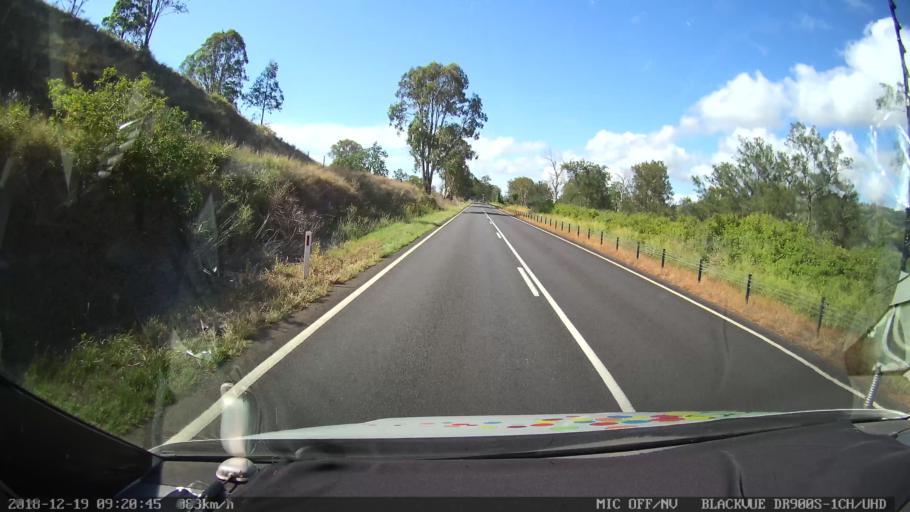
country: AU
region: New South Wales
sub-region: Kyogle
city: Kyogle
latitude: -28.5749
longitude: 152.9826
